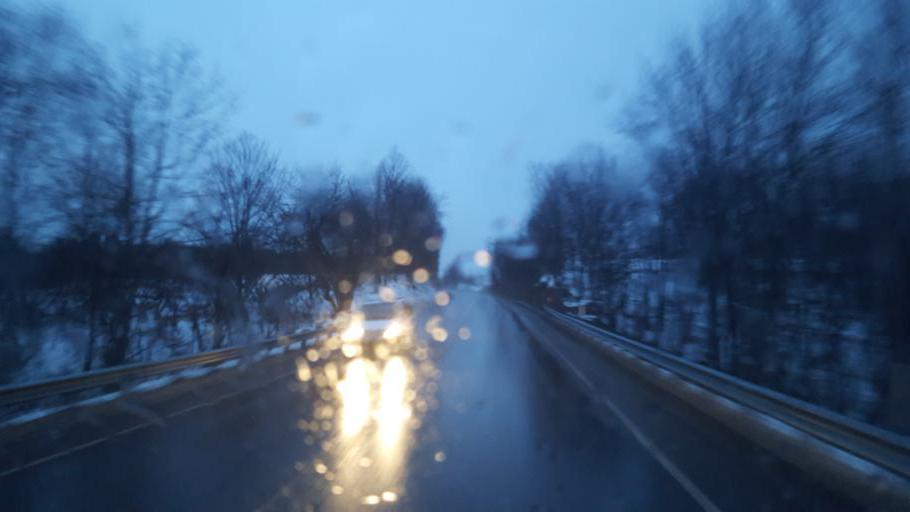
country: US
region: Pennsylvania
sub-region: McKean County
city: Port Allegany
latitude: 41.8265
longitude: -78.3451
